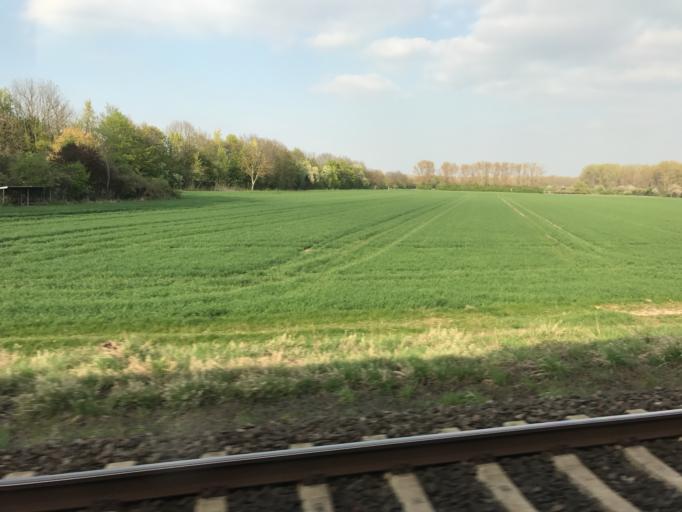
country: DE
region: Rheinland-Pfalz
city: Bodenheim
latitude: 49.9230
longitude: 8.3223
